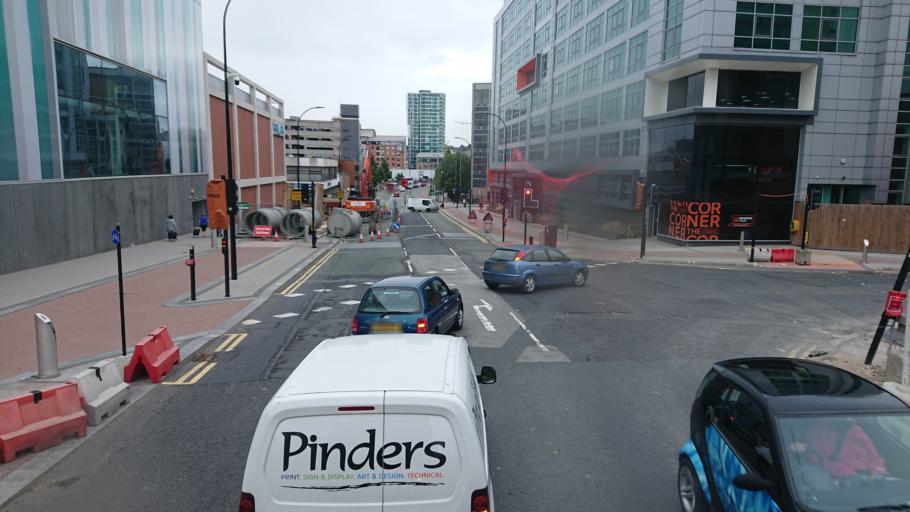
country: GB
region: England
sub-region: Sheffield
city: Sheffield
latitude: 53.3778
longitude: -1.4739
